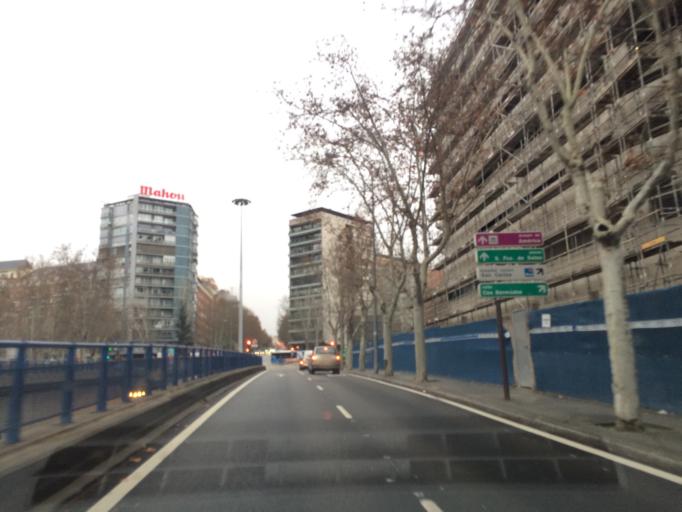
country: ES
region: Madrid
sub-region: Provincia de Madrid
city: Moncloa-Aravaca
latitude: 40.4384
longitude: -3.7187
